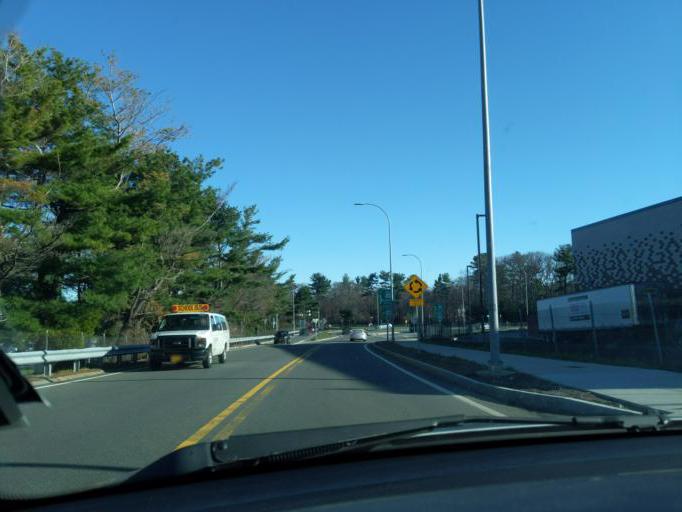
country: US
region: Massachusetts
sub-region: Essex County
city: Beverly
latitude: 42.5730
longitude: -70.8802
